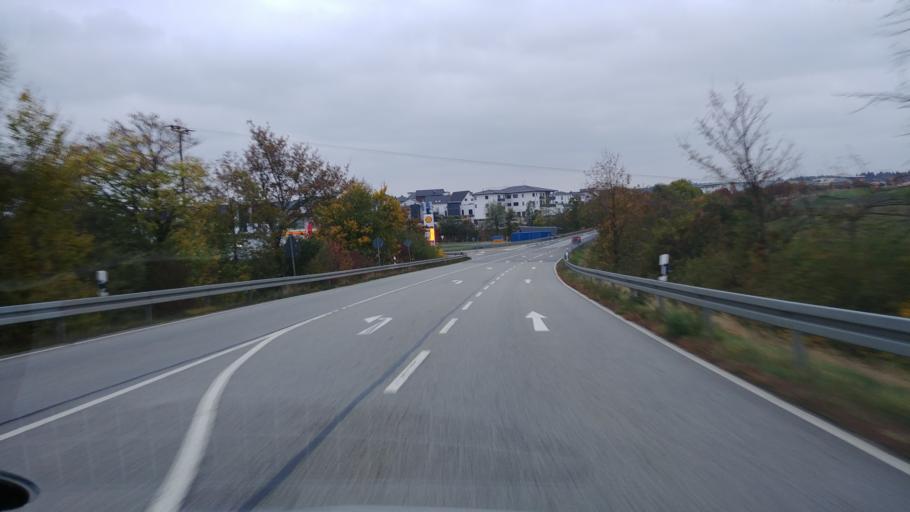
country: DE
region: Hesse
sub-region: Regierungsbezirk Darmstadt
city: Idstein
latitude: 50.2280
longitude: 8.1991
